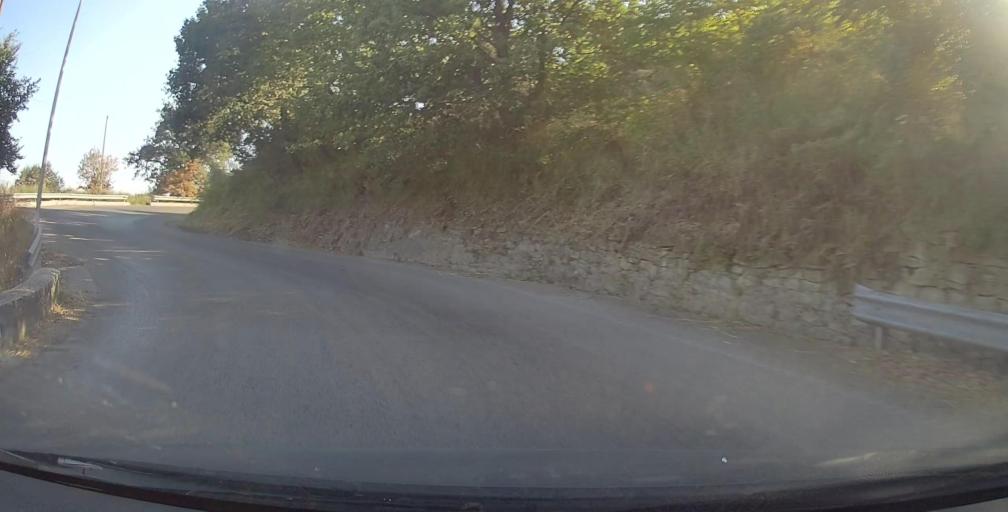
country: IT
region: Sicily
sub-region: Messina
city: San Piero Patti
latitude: 38.0765
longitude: 14.9788
